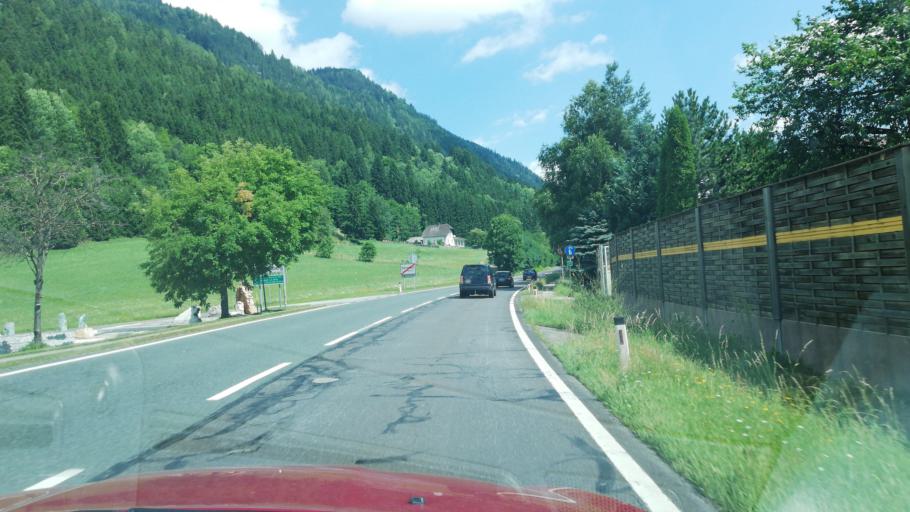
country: AT
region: Styria
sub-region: Politischer Bezirk Murau
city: Durnstein in der Steiermark
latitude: 46.9981
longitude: 14.3919
